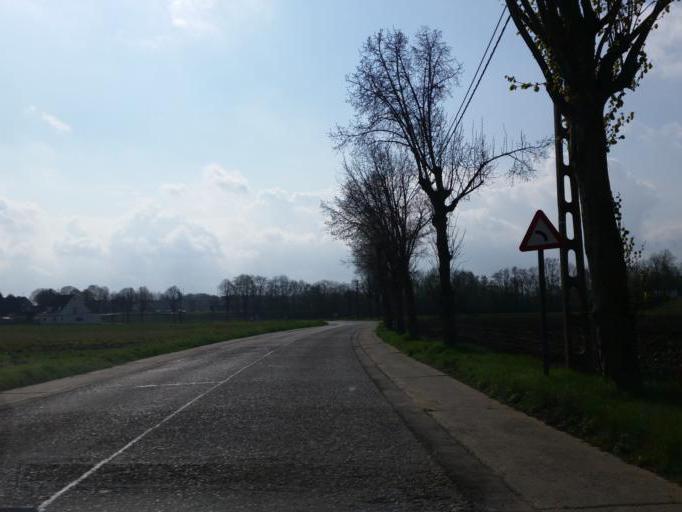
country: BE
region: Flanders
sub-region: Provincie Vlaams-Brabant
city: Bertem
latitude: 50.8644
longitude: 4.6132
